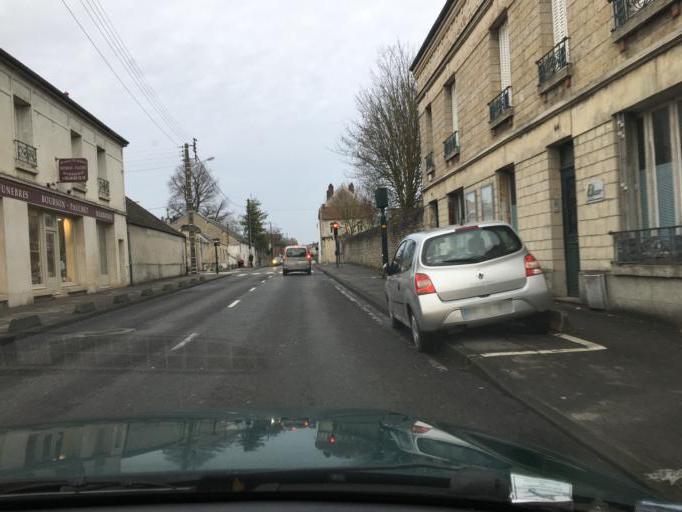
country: FR
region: Picardie
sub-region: Departement de l'Oise
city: Senlis
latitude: 49.1985
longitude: 2.5790
